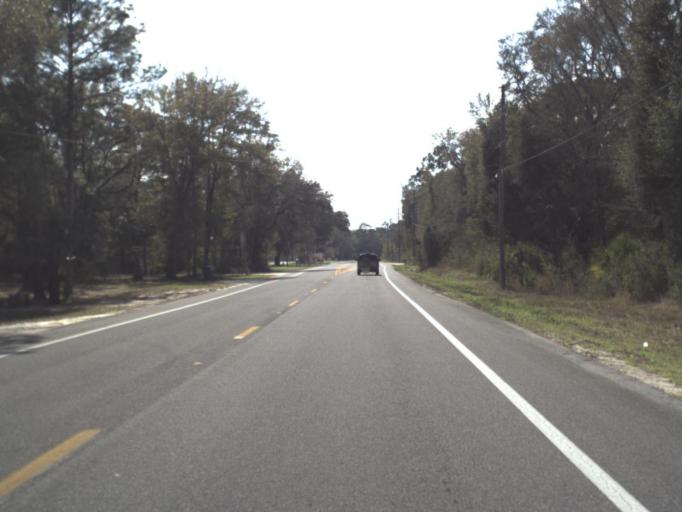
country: US
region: Florida
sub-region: Wakulla County
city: Crawfordville
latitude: 30.0740
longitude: -84.4351
